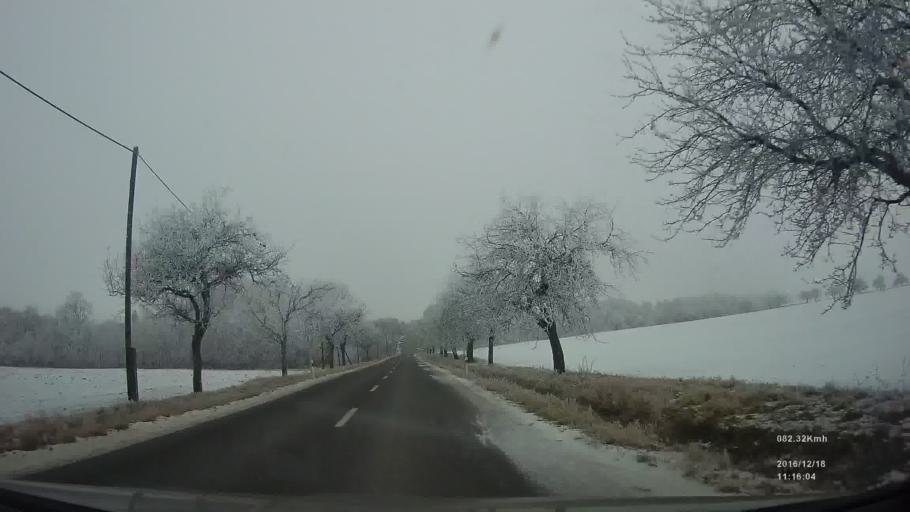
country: SK
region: Presovsky
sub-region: Okres Presov
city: Presov
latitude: 48.9131
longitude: 21.3248
